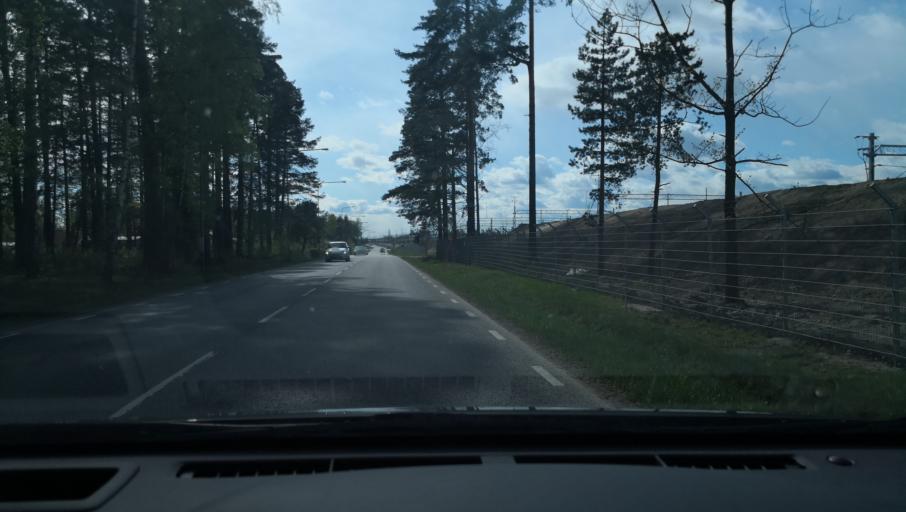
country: SE
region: OErebro
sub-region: Hallsbergs Kommun
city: Hallsberg
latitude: 59.0605
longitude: 15.0750
